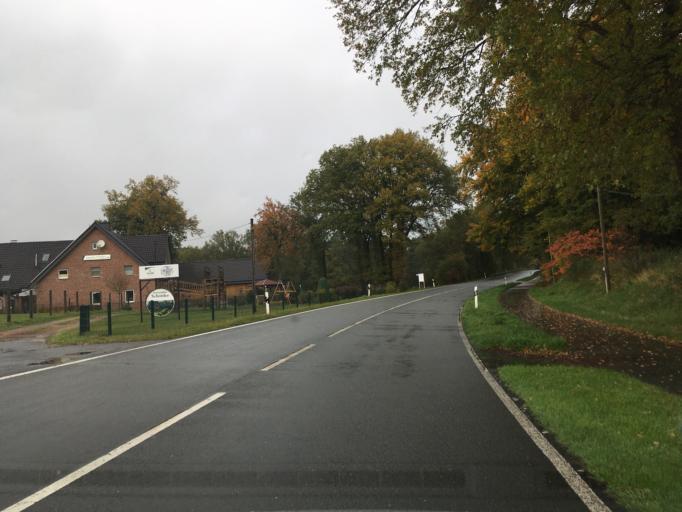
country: DE
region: North Rhine-Westphalia
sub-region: Regierungsbezirk Munster
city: Klein Reken
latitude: 51.8494
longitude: 7.0294
